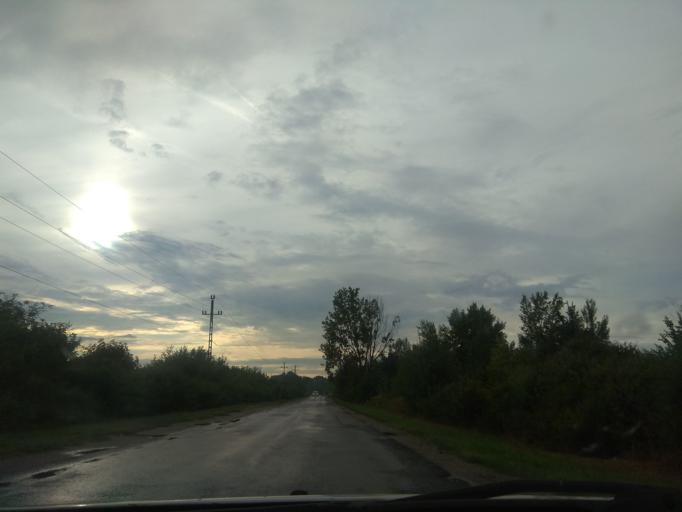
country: HU
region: Borsod-Abauj-Zemplen
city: Onga
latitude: 48.1189
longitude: 20.9287
